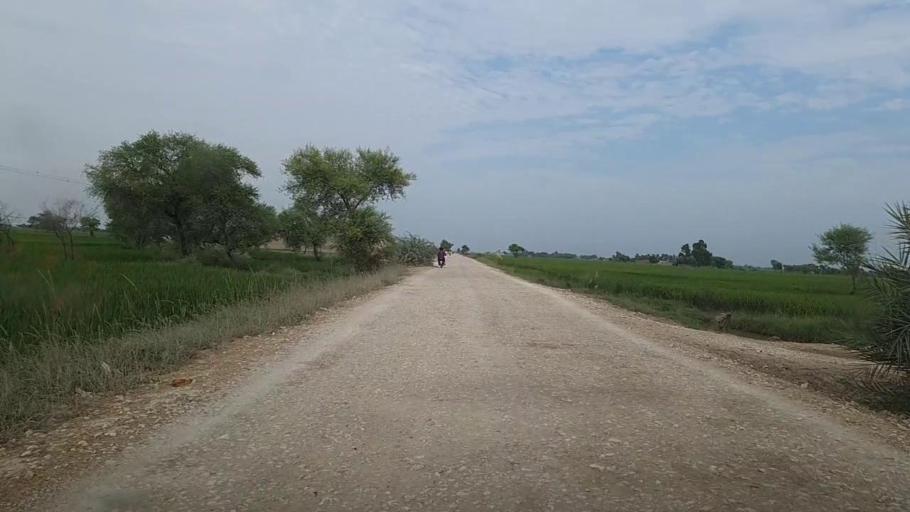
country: PK
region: Sindh
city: Thul
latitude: 28.2480
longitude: 68.7916
